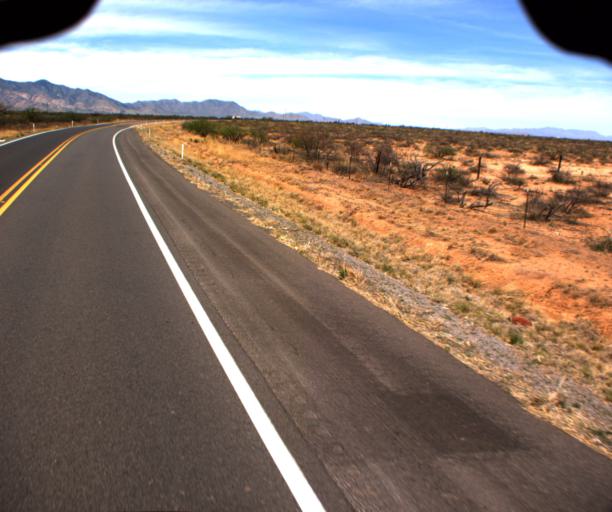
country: US
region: Arizona
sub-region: Cochise County
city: Tombstone
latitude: 31.9055
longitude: -109.8094
